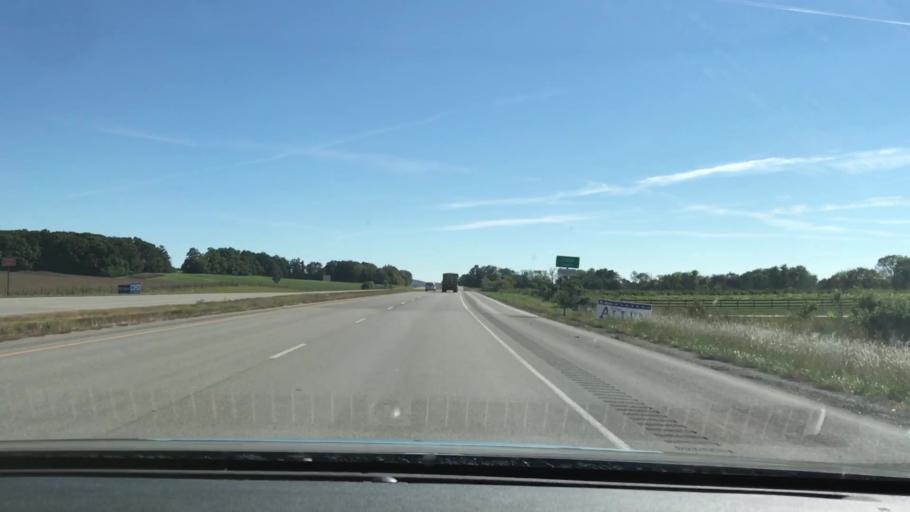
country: US
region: Kentucky
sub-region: Todd County
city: Elkton
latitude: 36.8469
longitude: -87.3002
